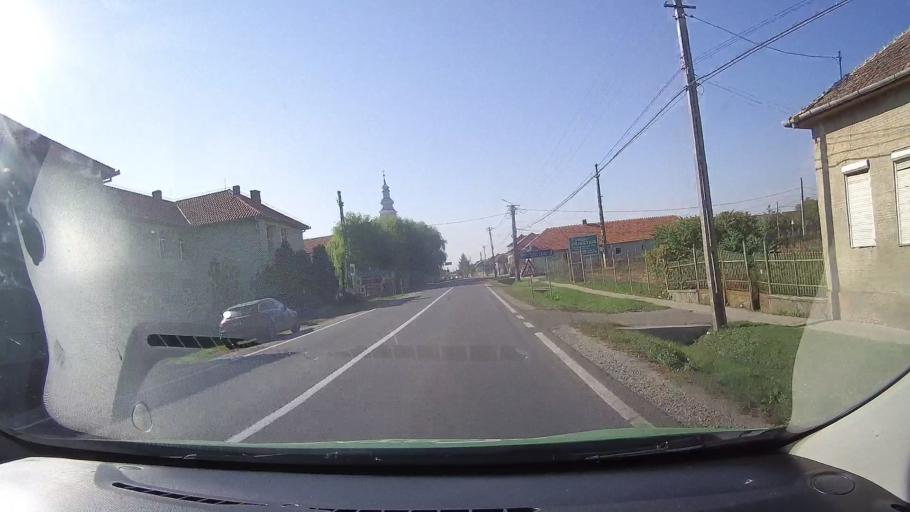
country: RO
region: Satu Mare
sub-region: Comuna Petresti
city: Petresti
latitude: 47.6056
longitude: 22.3634
